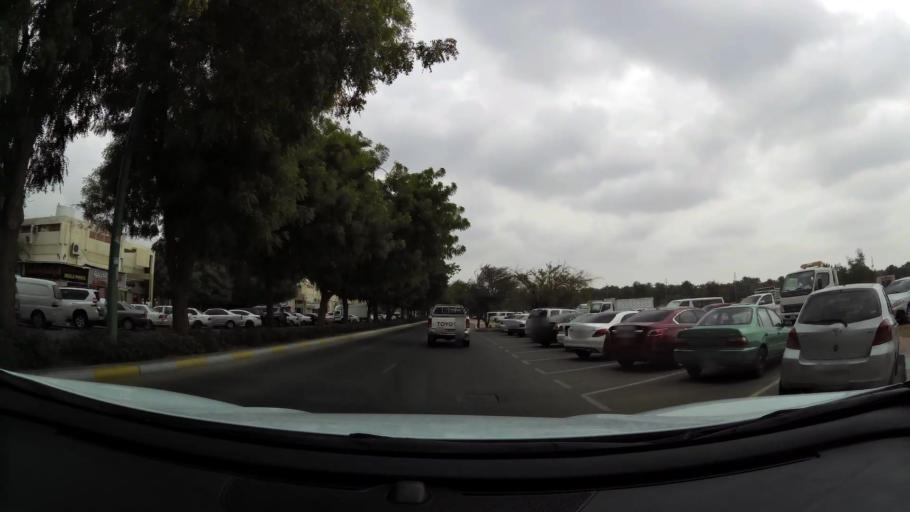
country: AE
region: Abu Dhabi
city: Al Ain
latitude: 24.2197
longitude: 55.7609
